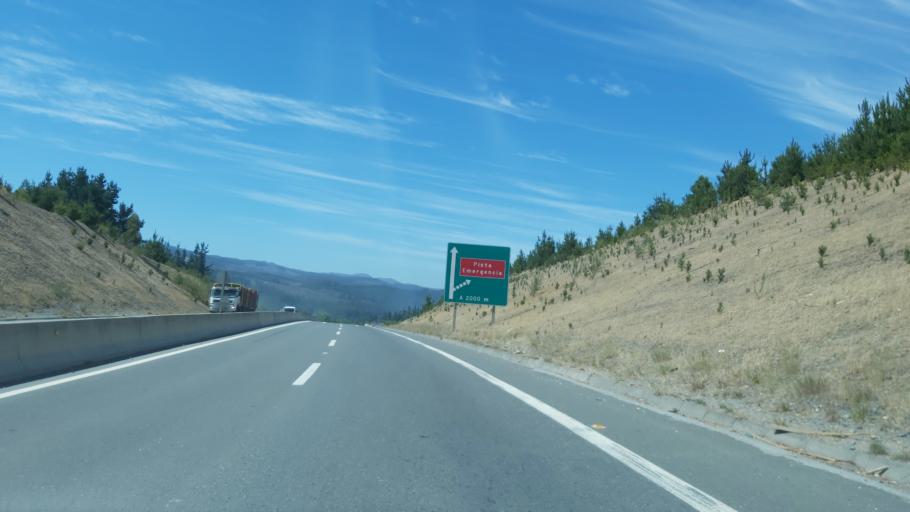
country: CL
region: Biobio
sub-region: Provincia de Concepcion
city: Lota
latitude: -37.0933
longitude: -73.1398
